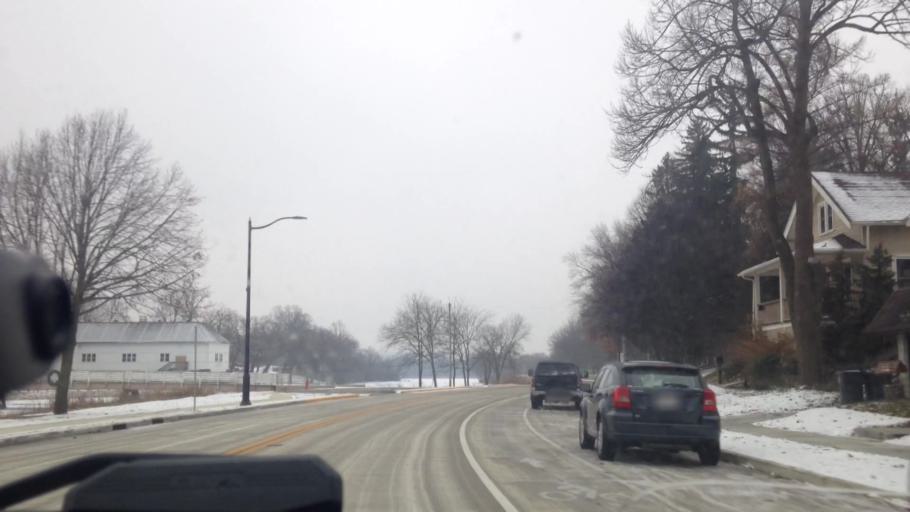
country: US
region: Wisconsin
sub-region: Dodge County
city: Mayville
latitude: 43.4909
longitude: -88.5446
